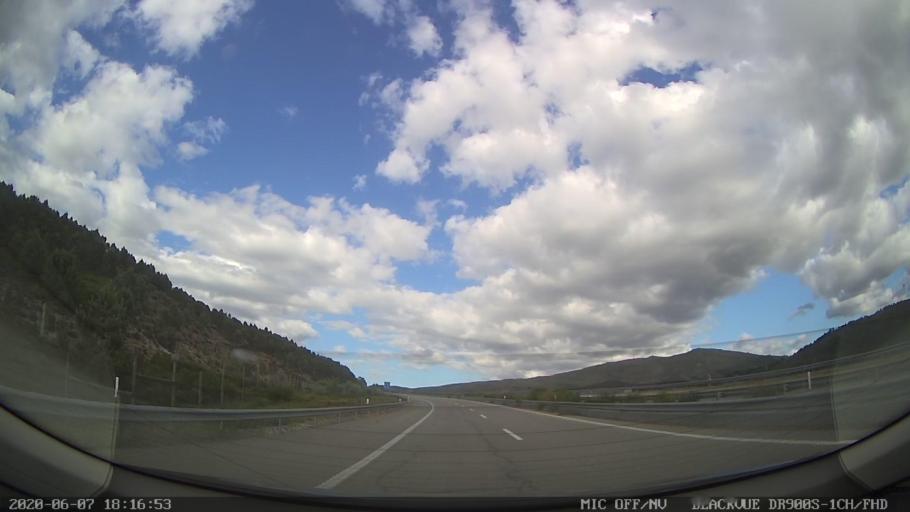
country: PT
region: Vila Real
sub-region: Ribeira de Pena
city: Ribeira de Pena
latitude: 41.4959
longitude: -7.8168
